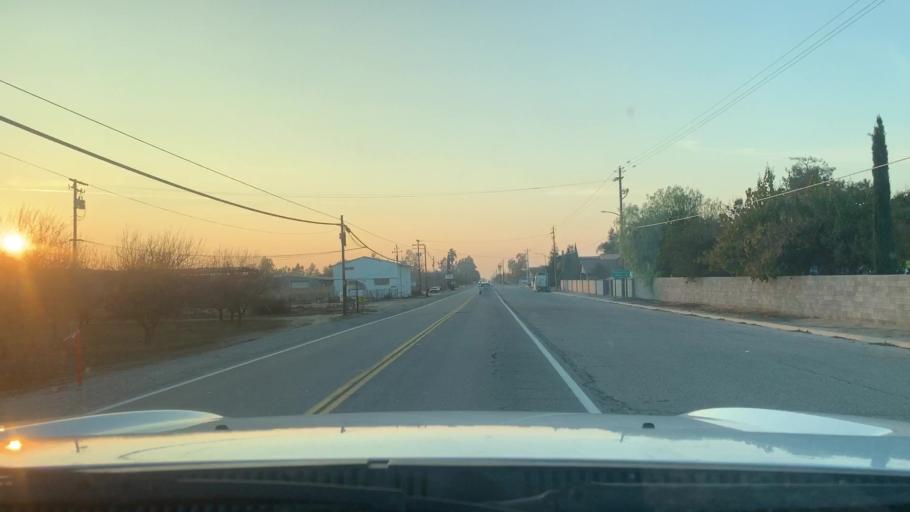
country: US
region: California
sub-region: Kern County
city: Rosedale
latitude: 35.3835
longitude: -119.2004
